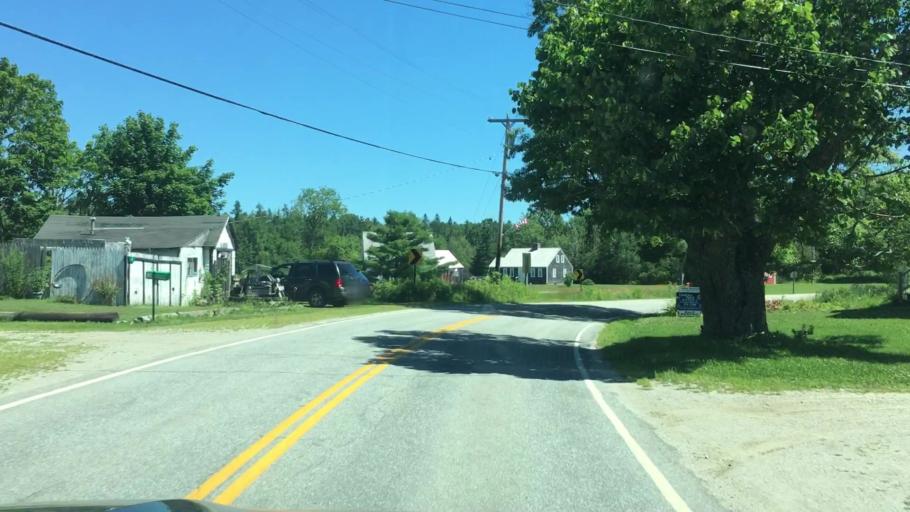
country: US
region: Maine
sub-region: Hancock County
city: Penobscot
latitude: 44.4689
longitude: -68.7082
